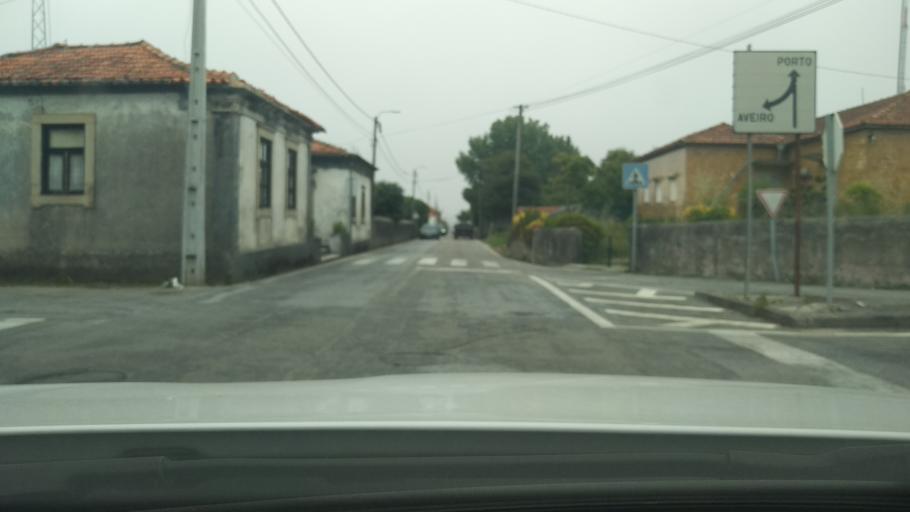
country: PT
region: Aveiro
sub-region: Espinho
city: Souto
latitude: 40.9871
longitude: -8.6252
